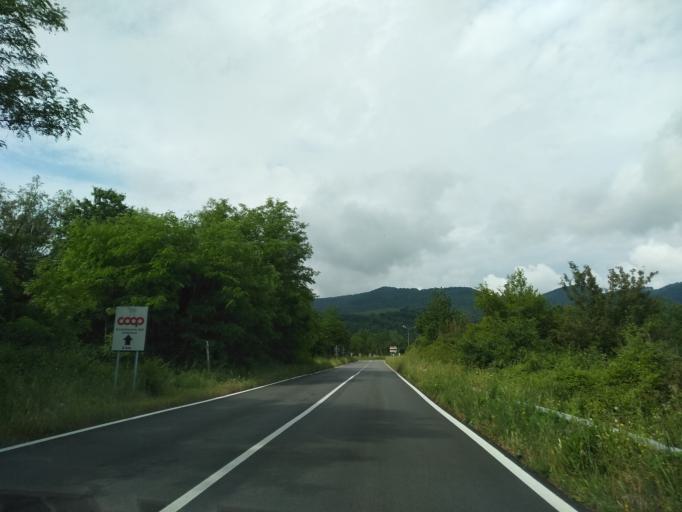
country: IT
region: Tuscany
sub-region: Province of Arezzo
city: Castelnuovo dei Sabbioni
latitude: 43.5595
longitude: 11.4539
